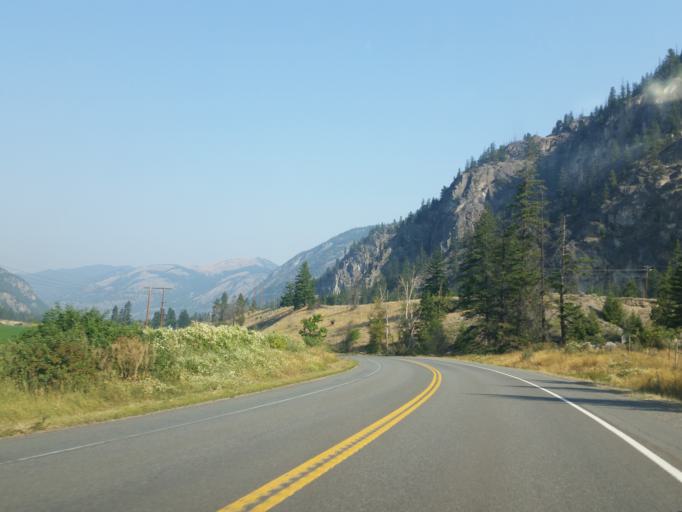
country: CA
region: British Columbia
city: Summerland
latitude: 49.3134
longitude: -120.0322
